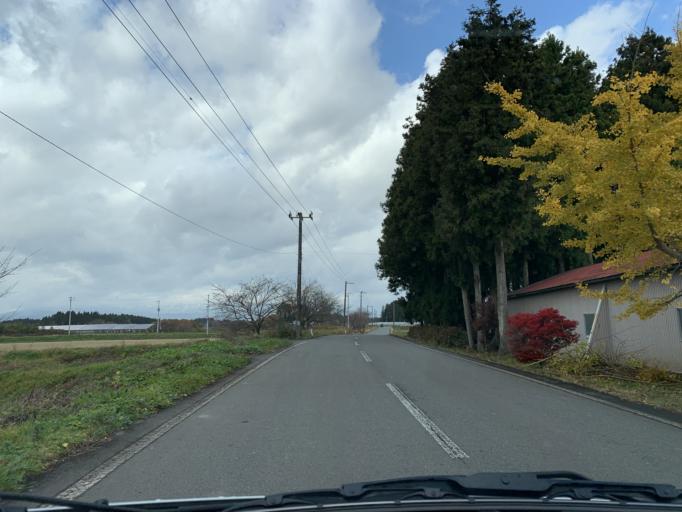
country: JP
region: Iwate
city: Mizusawa
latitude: 39.0668
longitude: 141.0791
